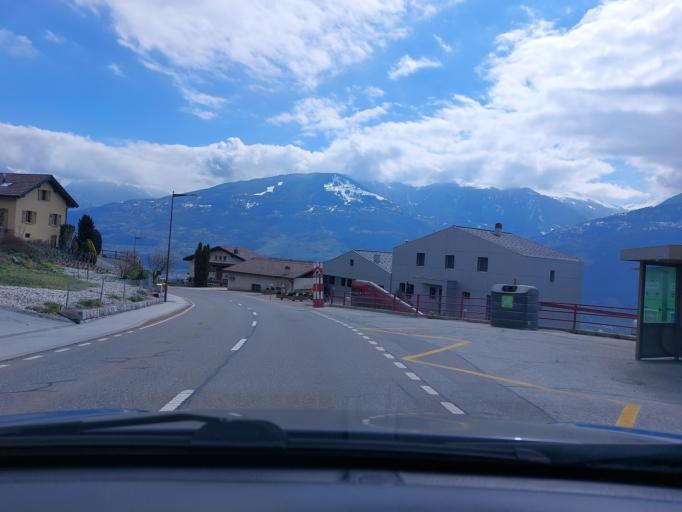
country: CH
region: Valais
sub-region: Conthey District
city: Vetroz
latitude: 46.2376
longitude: 7.2927
